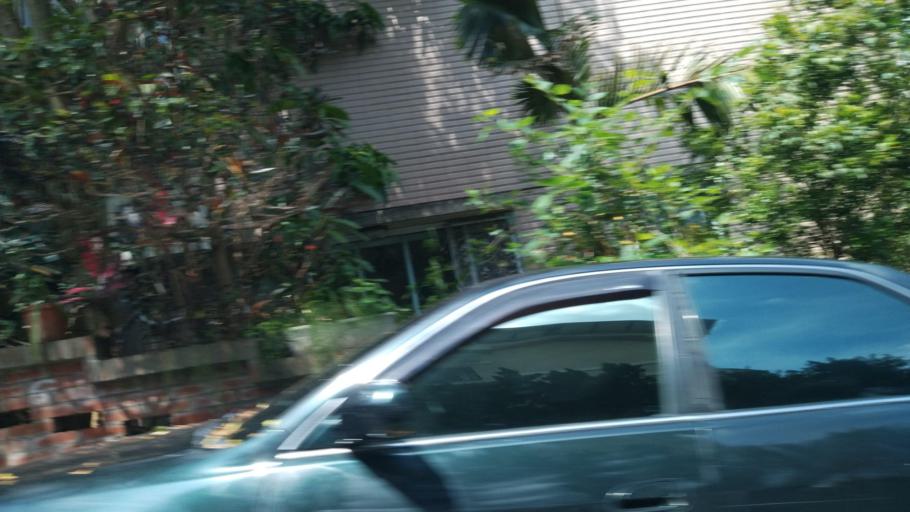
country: TW
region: Taipei
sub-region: Taipei
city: Banqiao
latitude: 24.9466
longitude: 121.5004
